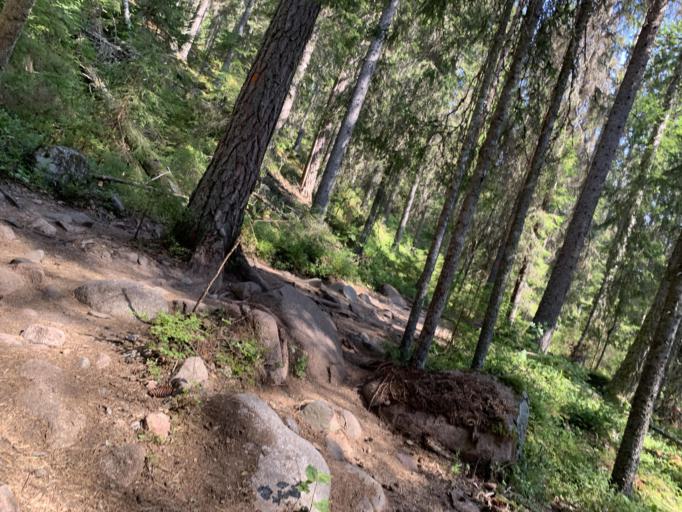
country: SE
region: Vaesternorrland
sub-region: OErnskoeldsviks Kommun
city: Kopmanholmen
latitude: 63.0880
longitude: 18.4908
